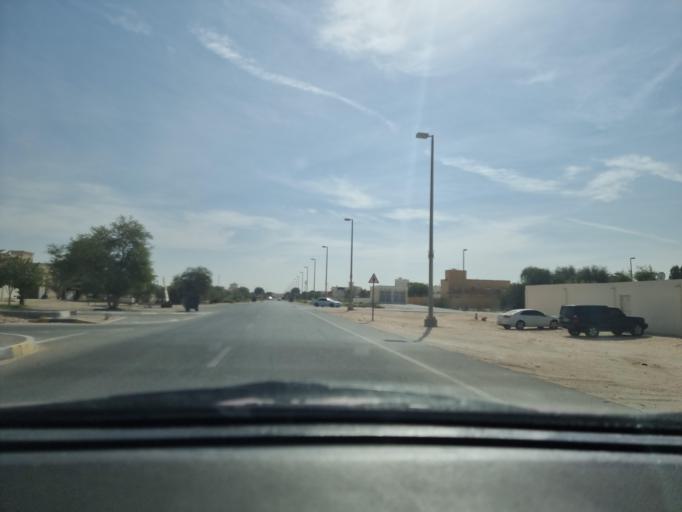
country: AE
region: Abu Dhabi
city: Abu Dhabi
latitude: 24.3835
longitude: 54.6998
